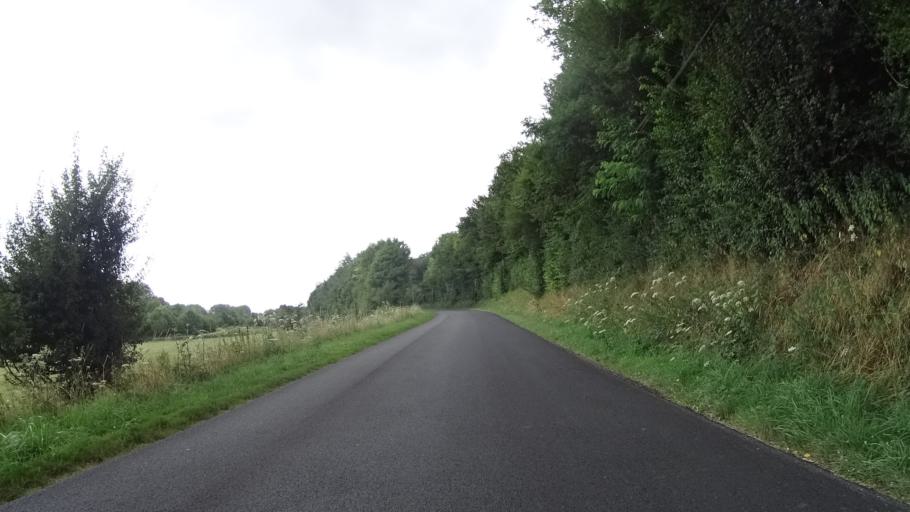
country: FR
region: Centre
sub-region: Departement du Loiret
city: Saint-Germain-des-Pres
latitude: 47.9260
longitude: 2.9008
